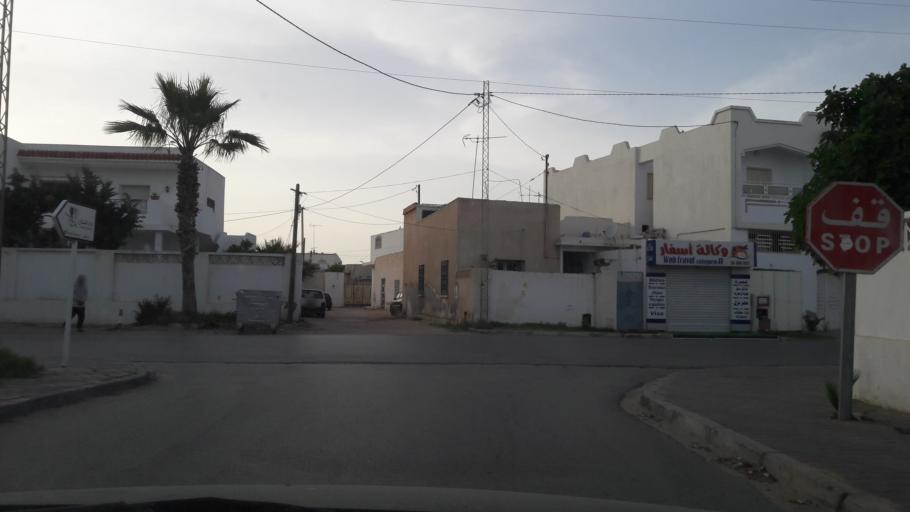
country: TN
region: Safaqis
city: Al Qarmadah
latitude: 34.8012
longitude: 10.7589
